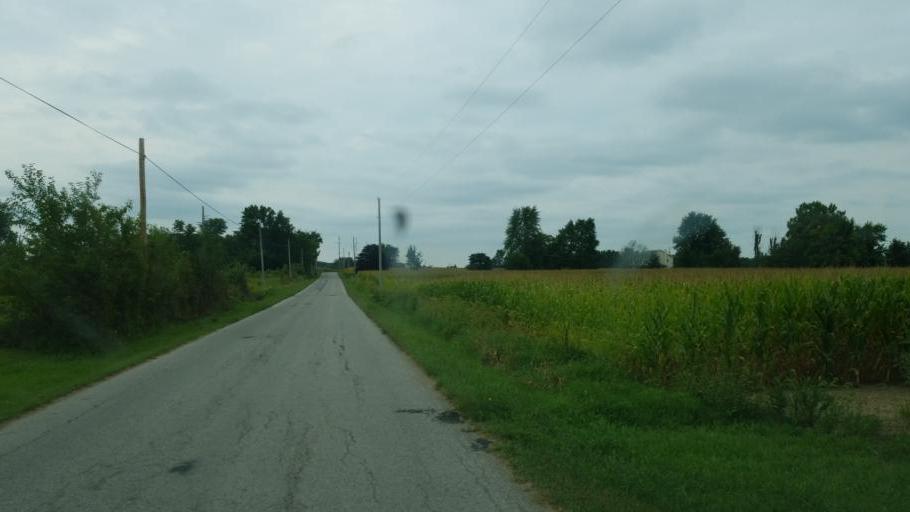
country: US
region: Ohio
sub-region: Morrow County
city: Mount Gilead
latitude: 40.6194
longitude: -82.8420
